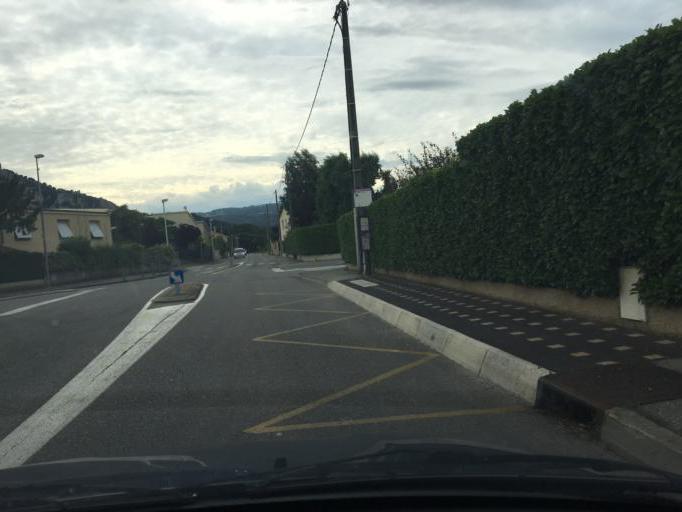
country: FR
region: Rhone-Alpes
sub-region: Departement de l'Ardeche
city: Guilherand-Granges
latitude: 44.9398
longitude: 4.8701
